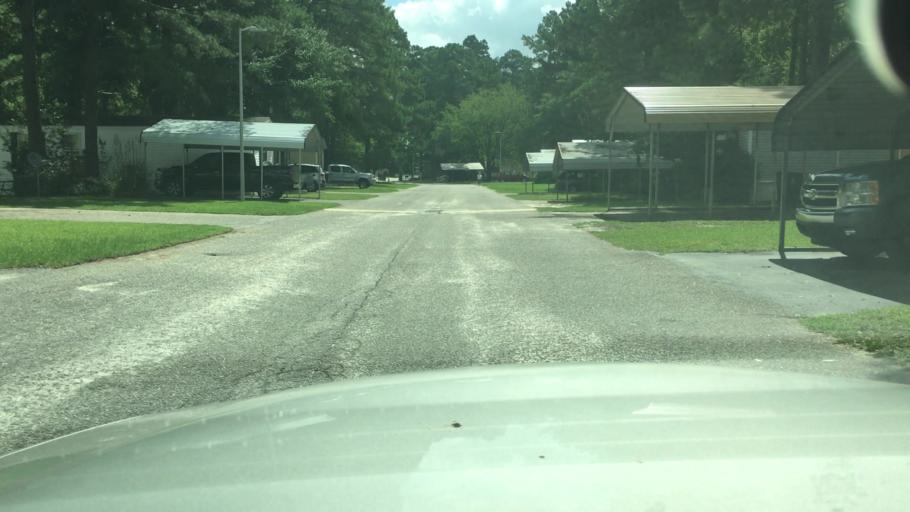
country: US
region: North Carolina
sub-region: Cumberland County
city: Fayetteville
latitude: 35.0052
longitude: -78.9036
